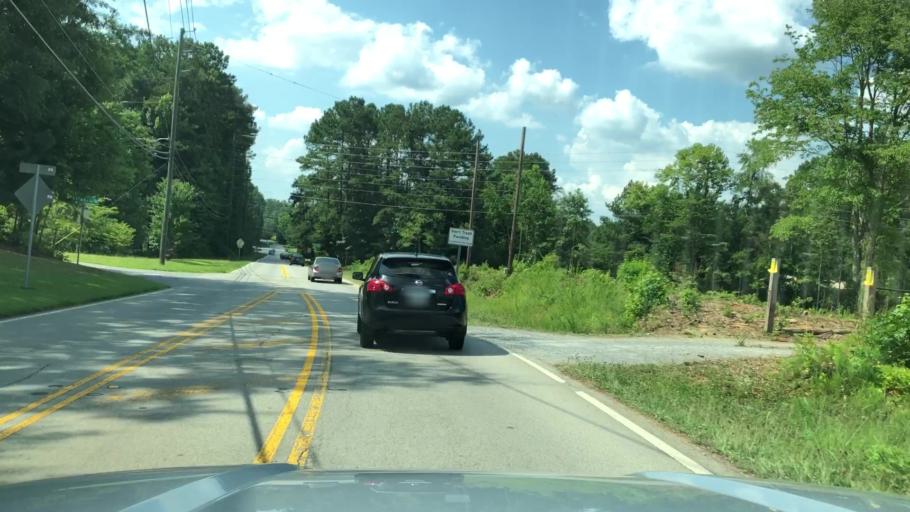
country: US
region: Georgia
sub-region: Paulding County
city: Dallas
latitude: 33.9618
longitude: -84.7903
